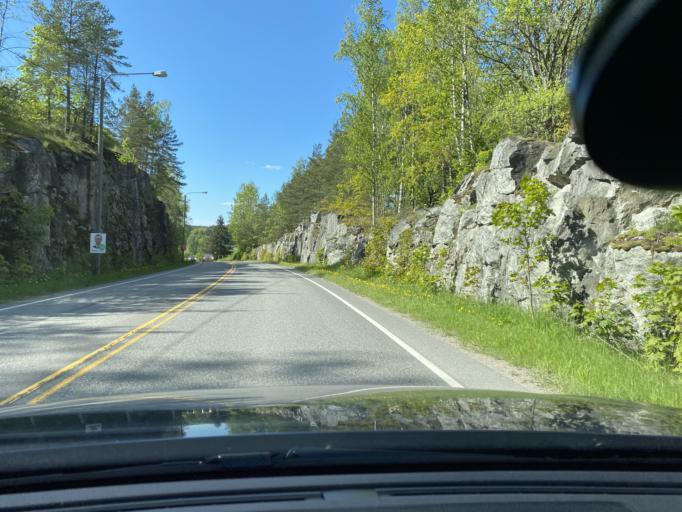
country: FI
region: Varsinais-Suomi
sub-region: Turku
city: Sauvo
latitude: 60.3491
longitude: 22.6807
